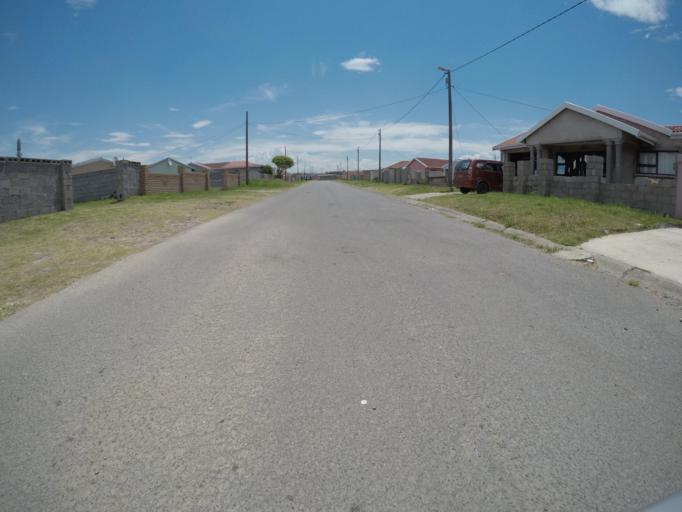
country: ZA
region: Eastern Cape
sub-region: Buffalo City Metropolitan Municipality
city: East London
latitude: -33.0495
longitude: 27.8508
